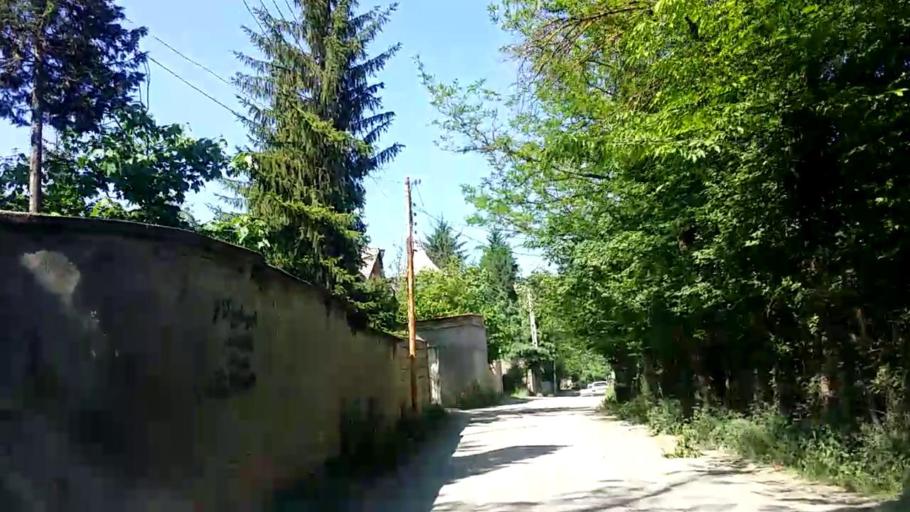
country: IR
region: Mazandaran
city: `Abbasabad
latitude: 36.5089
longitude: 51.1888
